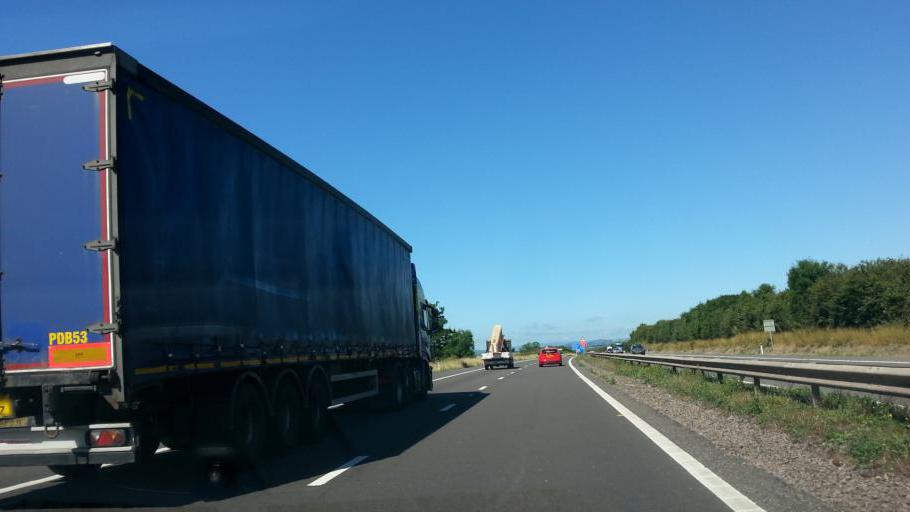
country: GB
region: England
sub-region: Herefordshire
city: Ross on Wye
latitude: 51.9289
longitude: -2.5524
